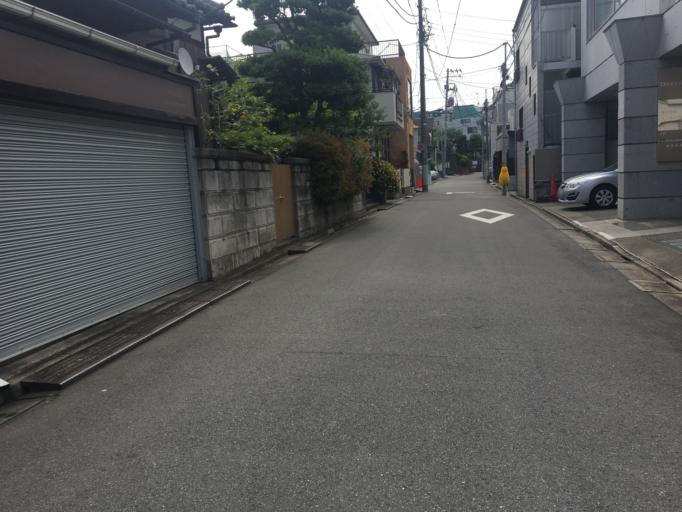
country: JP
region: Saitama
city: Kawaguchi
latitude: 35.7755
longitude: 139.7179
